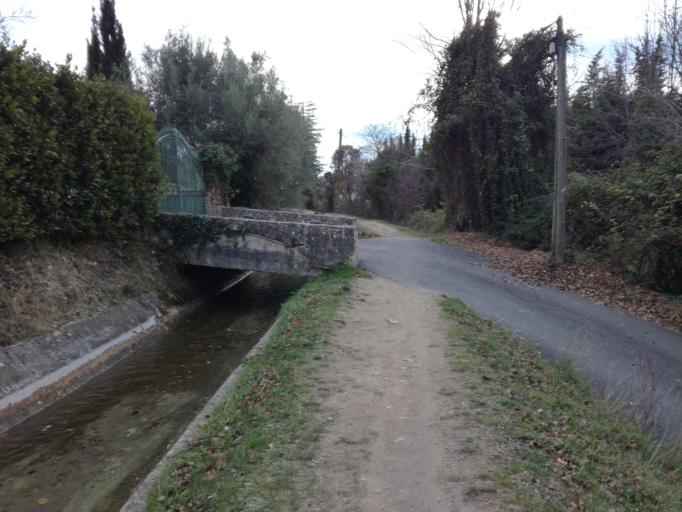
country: FR
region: Provence-Alpes-Cote d'Azur
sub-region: Departement des Alpes-Maritimes
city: Mouans-Sartoux
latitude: 43.6179
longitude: 6.9824
